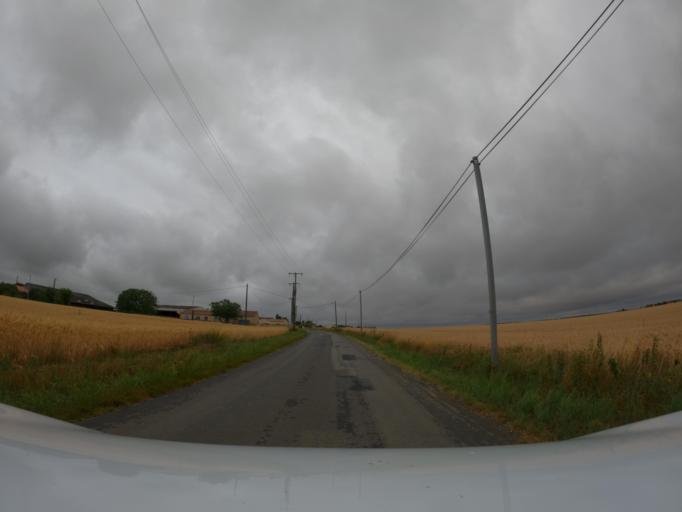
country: FR
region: Pays de la Loire
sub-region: Departement de la Vendee
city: Maillezais
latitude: 46.4050
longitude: -0.7312
